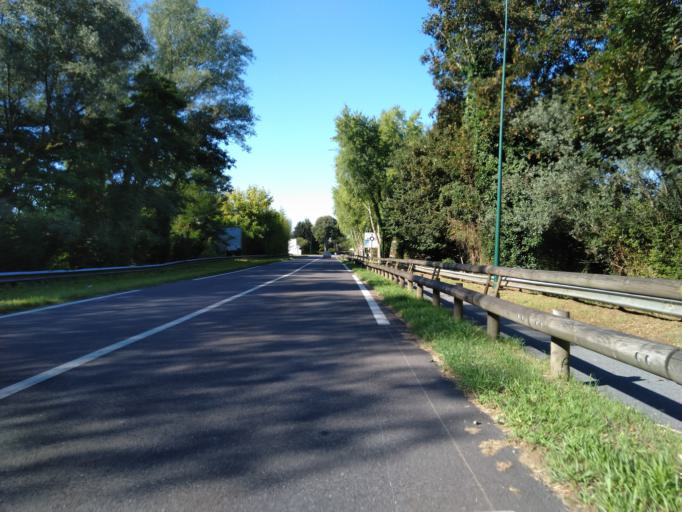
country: FR
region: Aquitaine
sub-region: Departement des Landes
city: Saint-Paul-les-Dax
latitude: 43.7321
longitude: -1.0346
